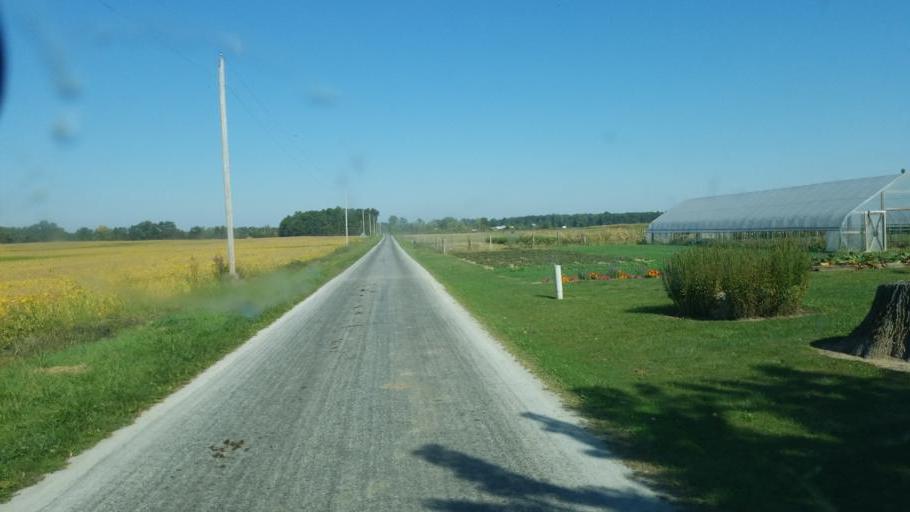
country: US
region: Ohio
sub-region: Hardin County
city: Kenton
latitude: 40.5678
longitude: -83.4875
